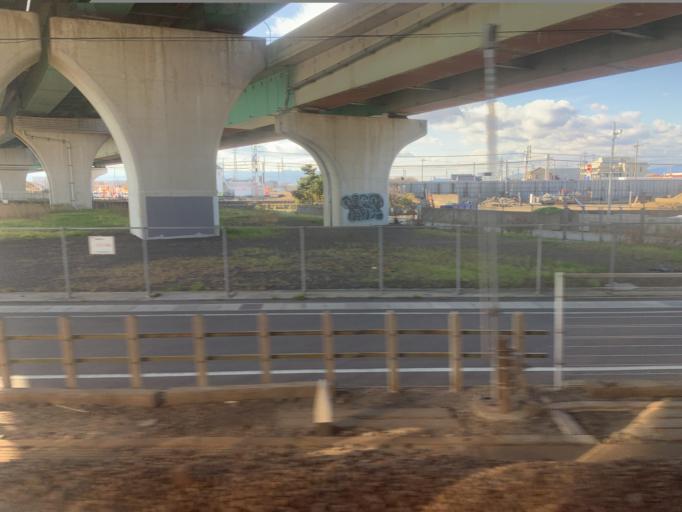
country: JP
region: Aichi
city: Kuroda
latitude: 35.3364
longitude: 136.7819
